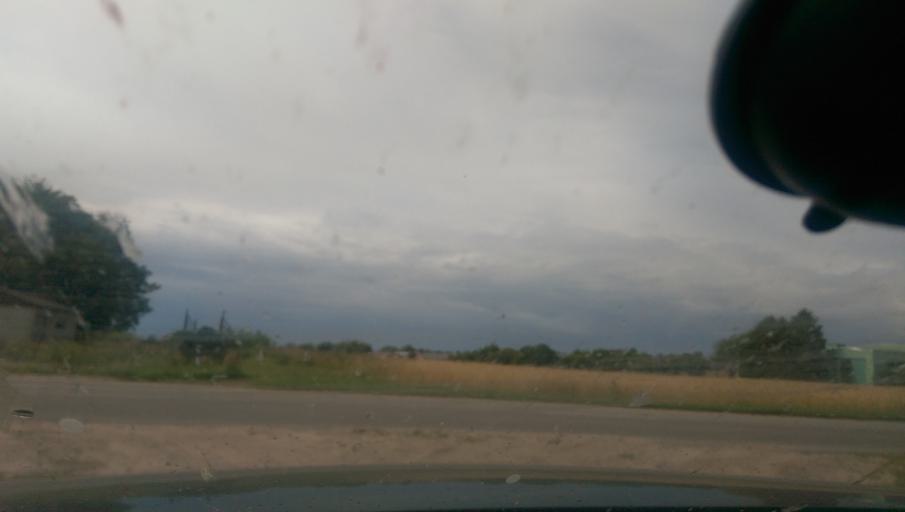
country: LT
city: Rusne
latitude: 55.2923
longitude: 21.3686
